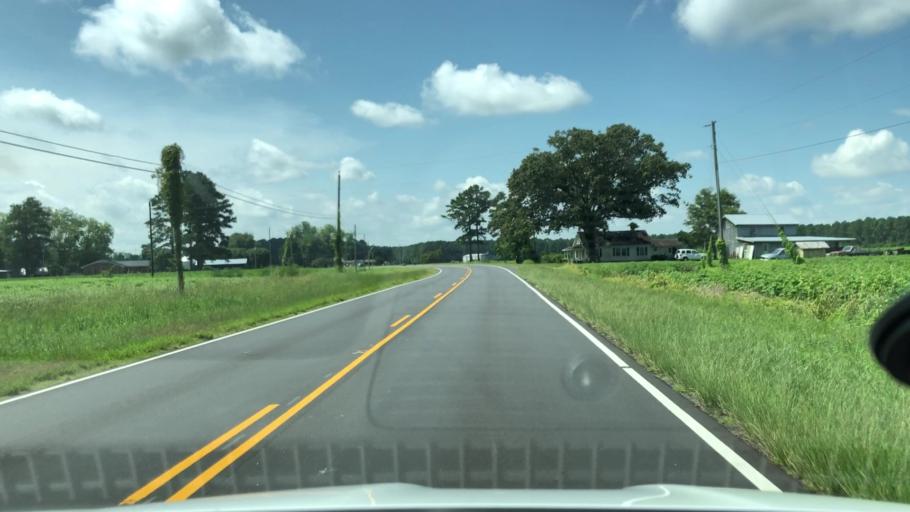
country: US
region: North Carolina
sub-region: Martin County
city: Williamston
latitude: 35.7655
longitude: -77.0733
